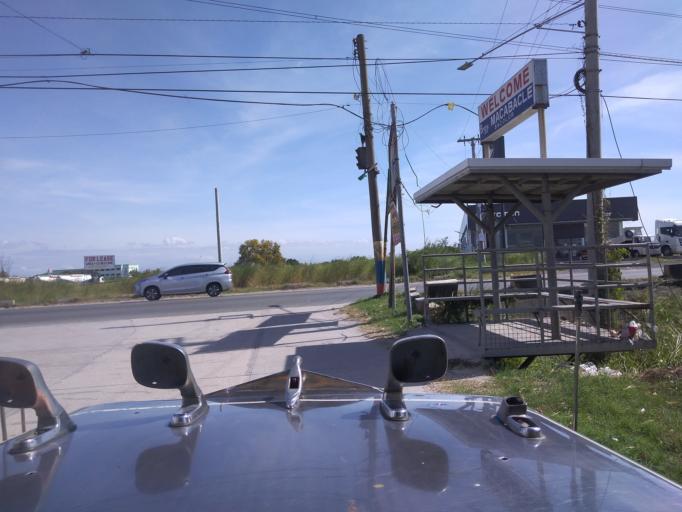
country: PH
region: Central Luzon
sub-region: Province of Pampanga
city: San Juan
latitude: 15.0208
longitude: 120.6681
